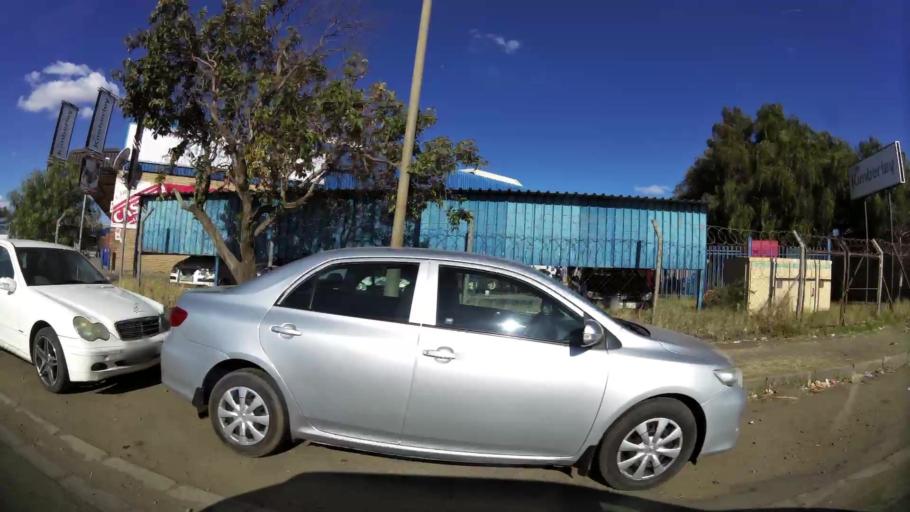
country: ZA
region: Northern Cape
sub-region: Frances Baard District Municipality
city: Kimberley
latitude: -28.7313
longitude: 24.7608
